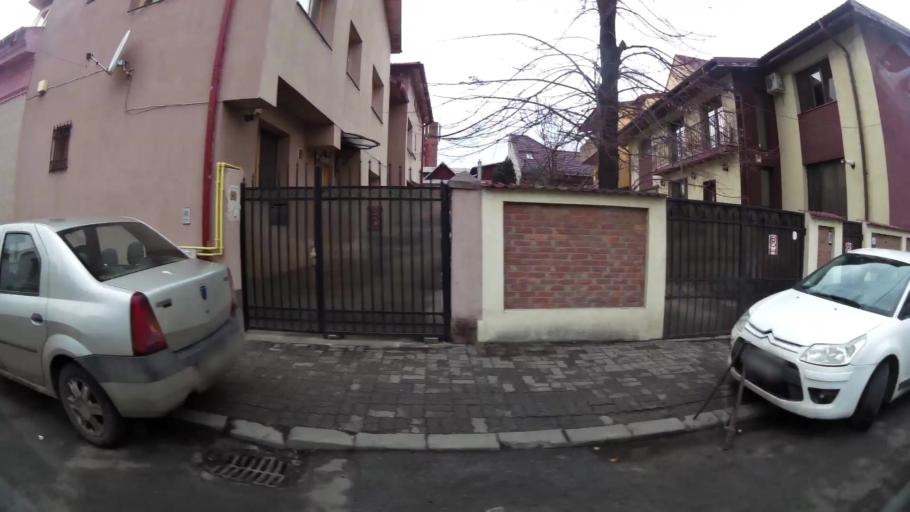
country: RO
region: Bucuresti
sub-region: Municipiul Bucuresti
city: Bucuresti
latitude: 44.4554
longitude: 26.0748
